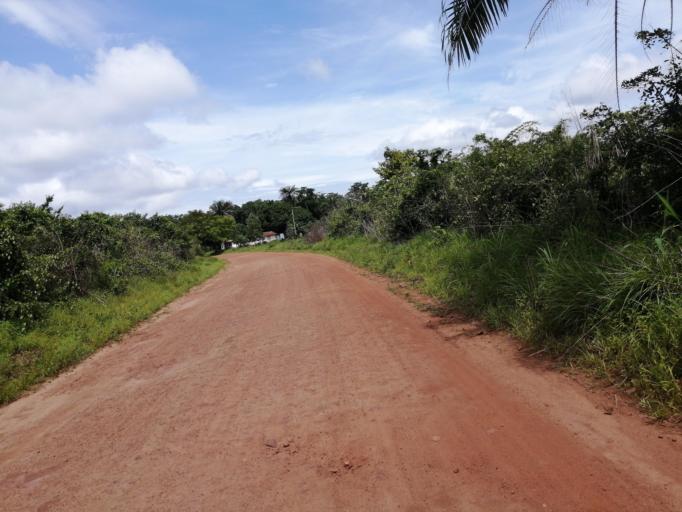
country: SL
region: Northern Province
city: Pepel
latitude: 8.6208
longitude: -13.0414
